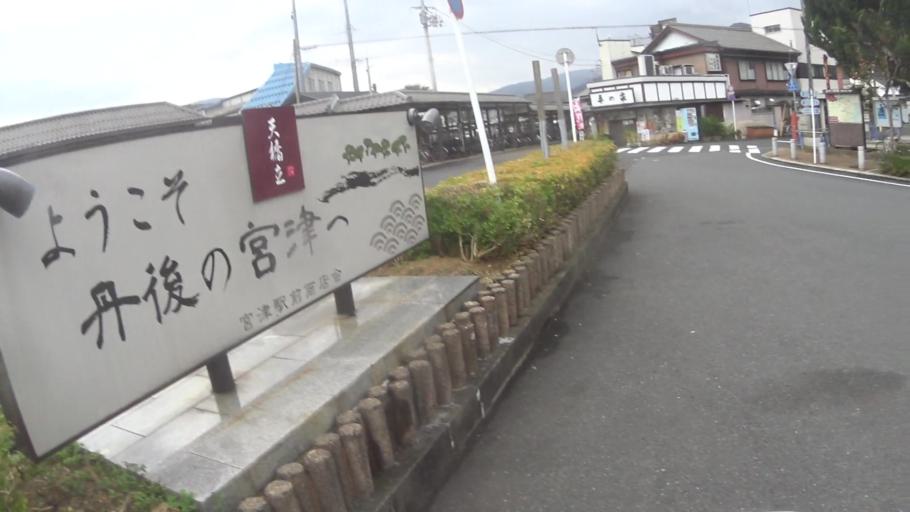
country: JP
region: Kyoto
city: Miyazu
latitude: 35.5346
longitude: 135.1995
